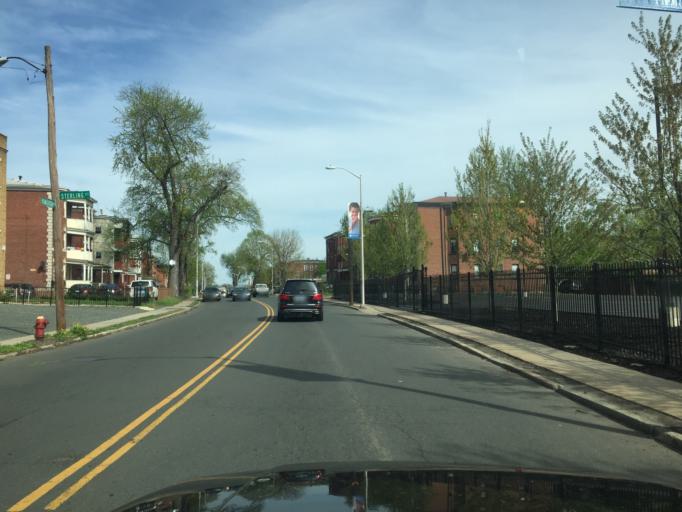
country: US
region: Connecticut
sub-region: Hartford County
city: Hartford
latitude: 41.7780
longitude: -72.6962
